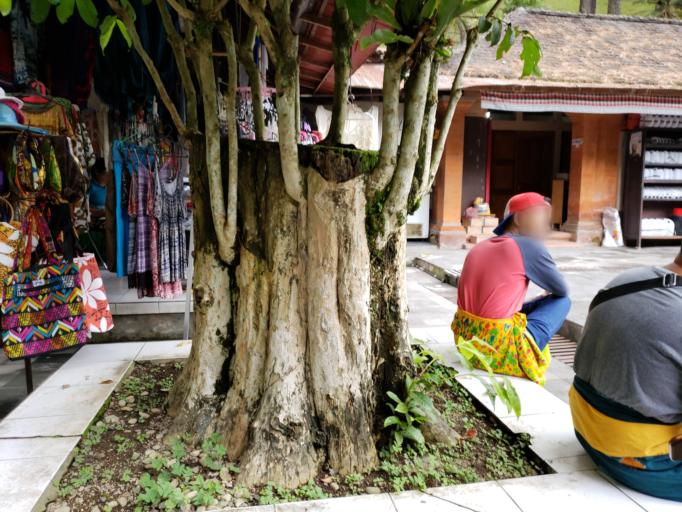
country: ID
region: Bali
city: Banjar Manukayaanyar
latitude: -8.4150
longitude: 115.3157
